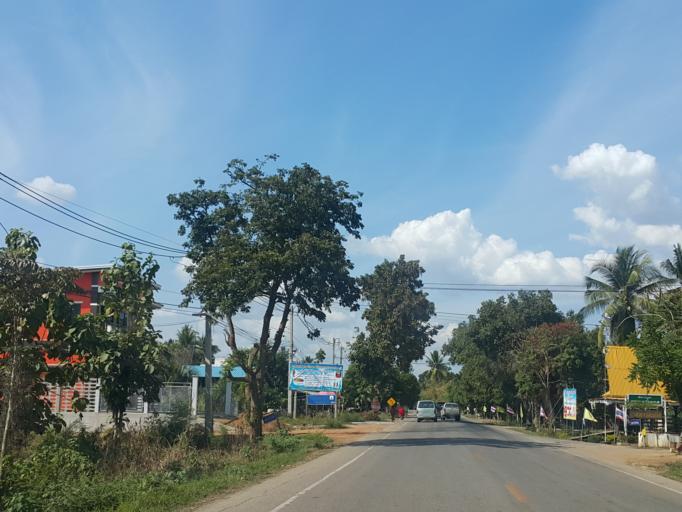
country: TH
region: Sukhothai
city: Sawankhalok
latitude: 17.2906
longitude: 99.8322
